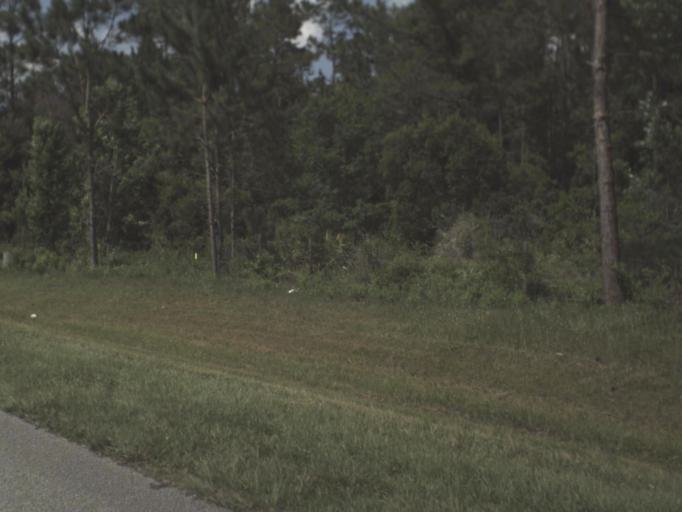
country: US
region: Florida
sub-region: Alachua County
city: Waldo
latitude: 29.8233
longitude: -82.1675
